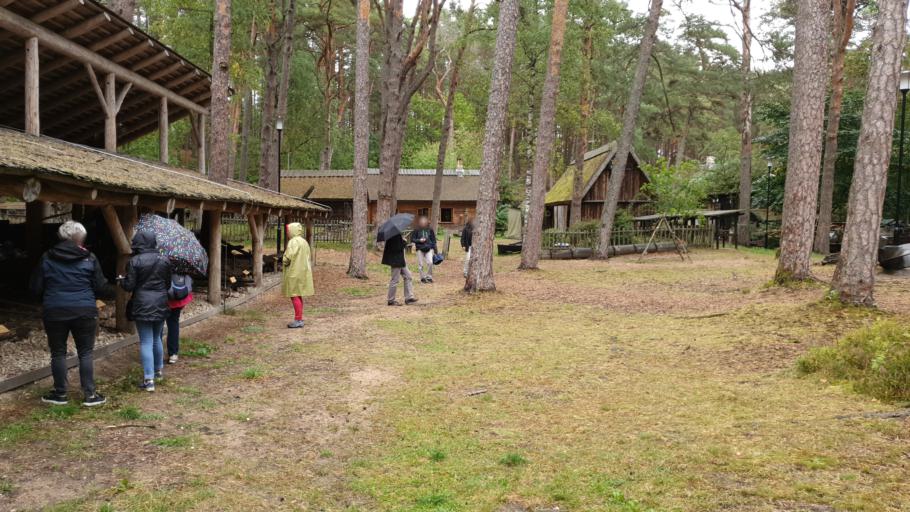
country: LV
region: Babite
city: Pinki
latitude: 56.9963
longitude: 23.9155
